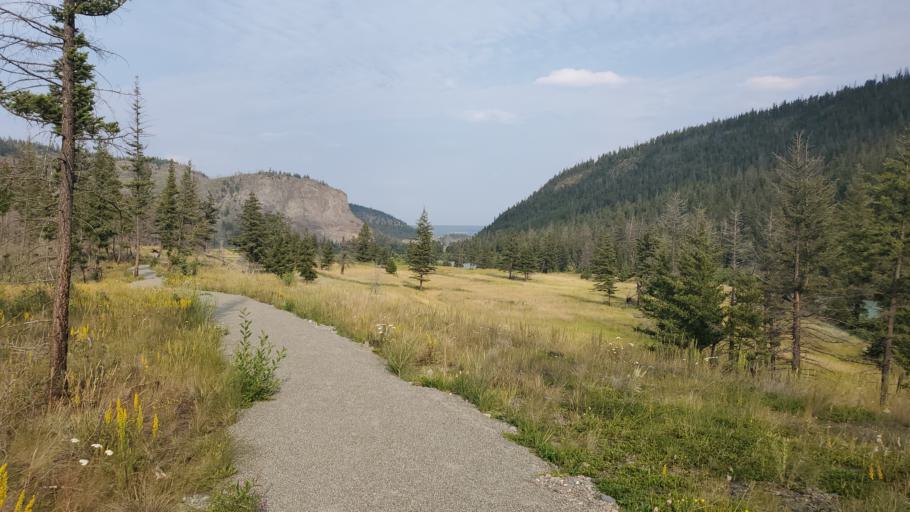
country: CA
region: British Columbia
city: Hanceville
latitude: 52.0864
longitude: -123.3873
